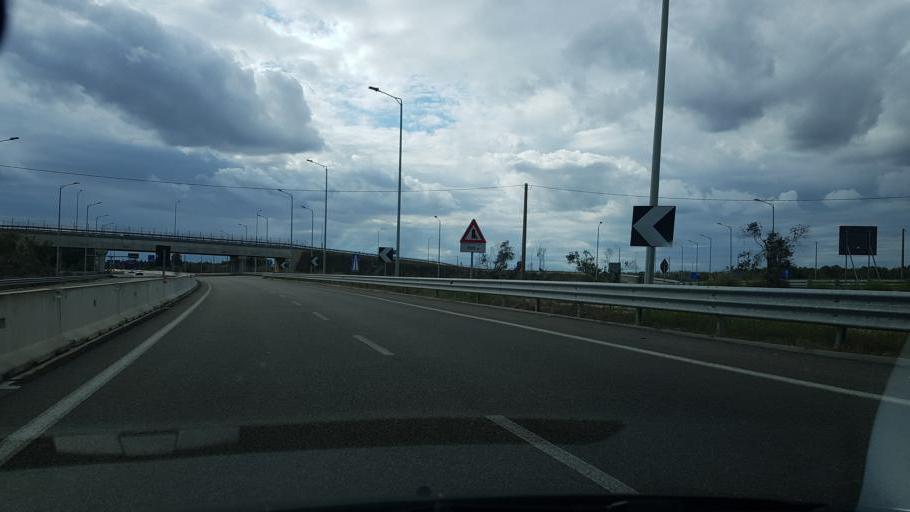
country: IT
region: Apulia
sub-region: Provincia di Lecce
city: Palmariggi
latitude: 40.1283
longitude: 18.3680
